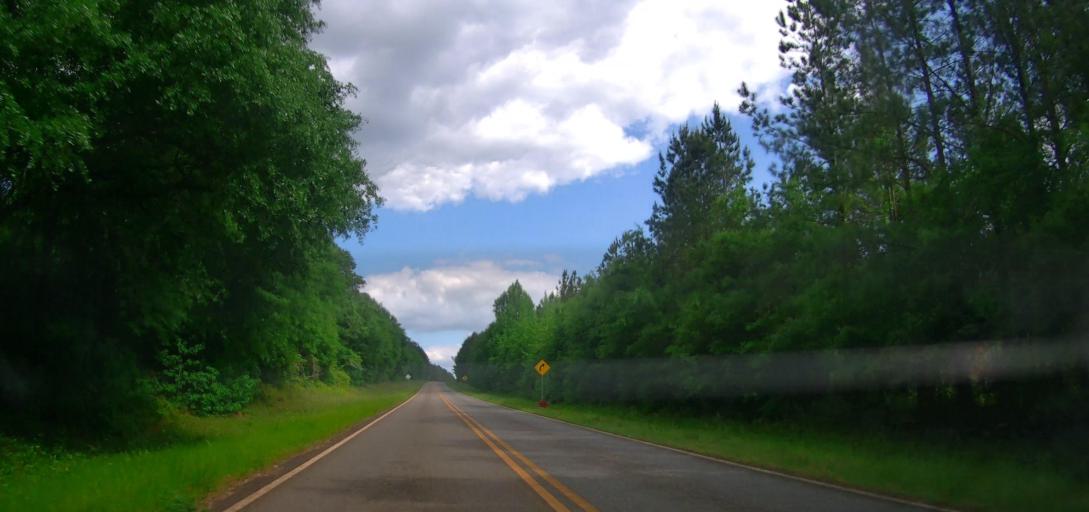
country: US
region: Georgia
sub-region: Laurens County
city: East Dublin
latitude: 32.7391
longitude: -82.9182
